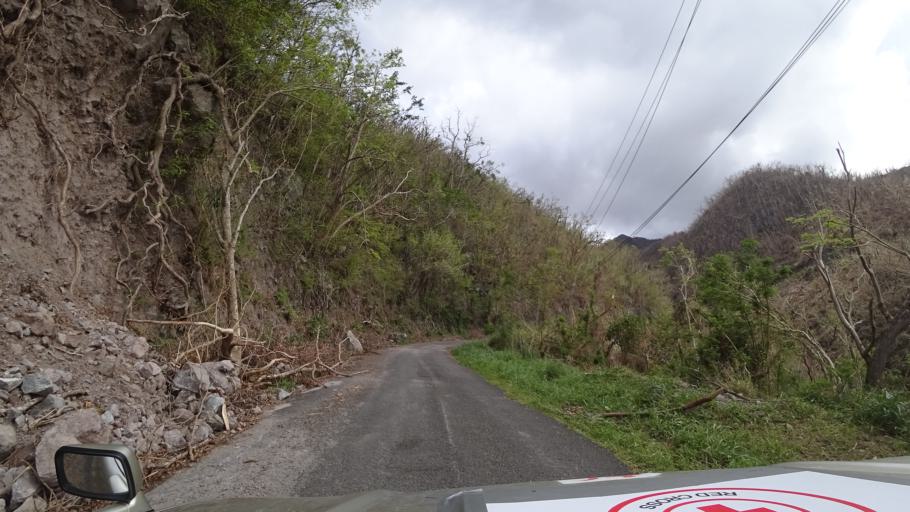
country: DM
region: Saint Mark
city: Soufriere
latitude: 15.2416
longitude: -61.3677
